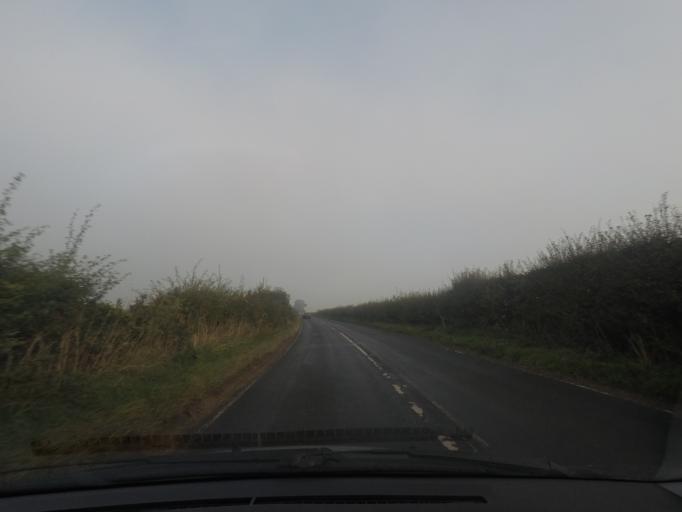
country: GB
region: England
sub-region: City and Borough of Leeds
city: Walton
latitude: 54.0190
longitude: -1.3123
